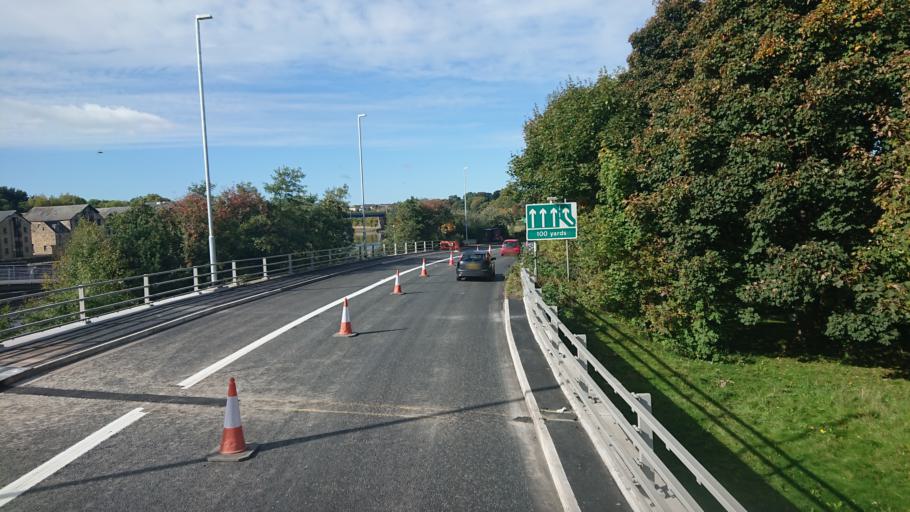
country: GB
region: England
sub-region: Lancashire
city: Lancaster
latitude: 54.0527
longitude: -2.8013
